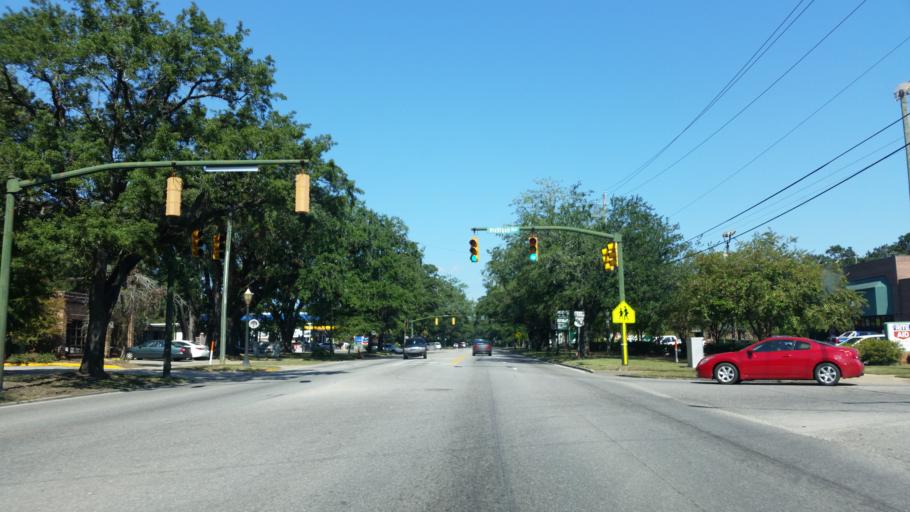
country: US
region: Alabama
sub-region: Mobile County
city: Mobile
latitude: 30.6819
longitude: -88.0677
